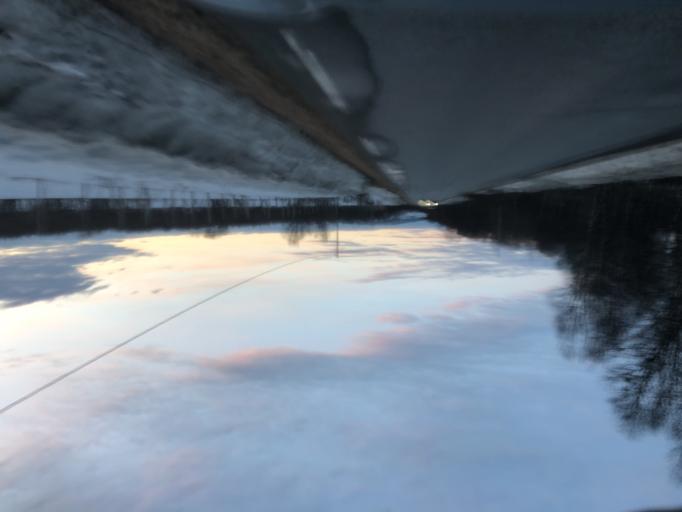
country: NO
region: Sor-Trondelag
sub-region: Tydal
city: Aas
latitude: 62.6765
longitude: 11.8419
